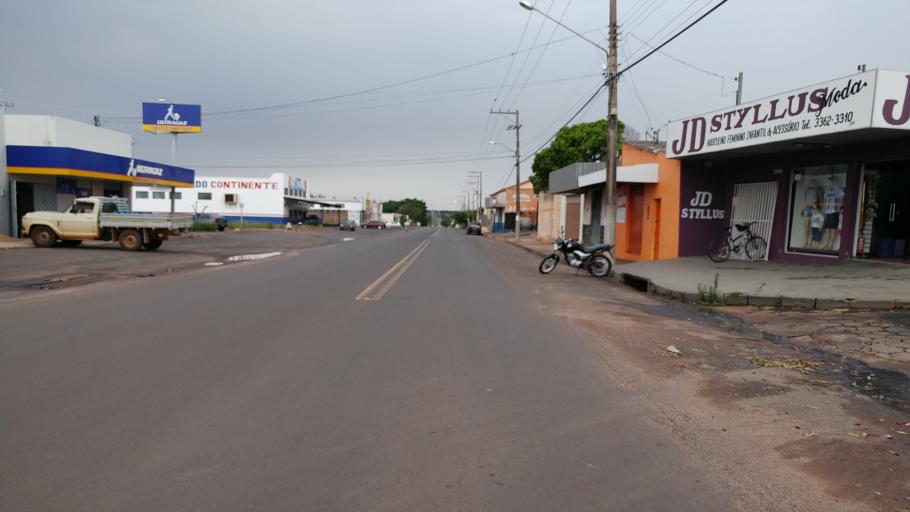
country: BR
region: Sao Paulo
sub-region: Paraguacu Paulista
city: Paraguacu Paulista
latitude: -22.4311
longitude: -50.5790
